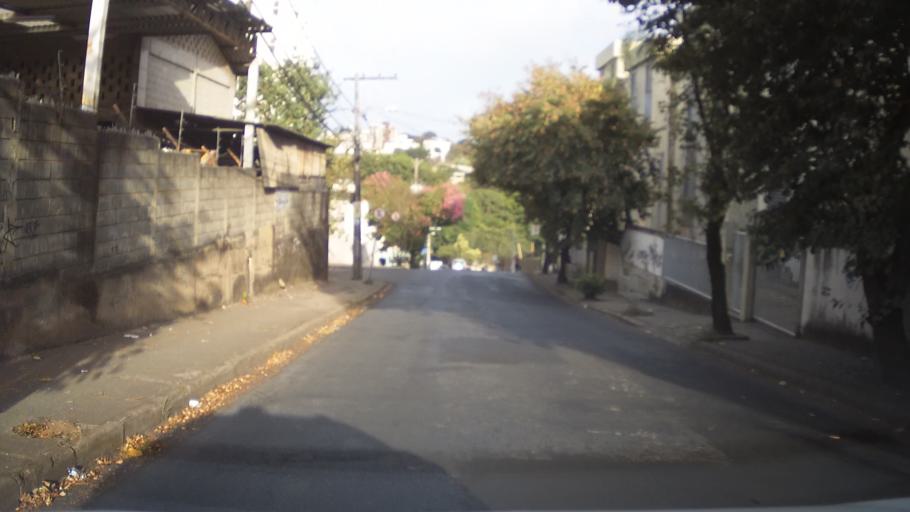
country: BR
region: Minas Gerais
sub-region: Belo Horizonte
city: Belo Horizonte
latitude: -19.8684
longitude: -43.9831
